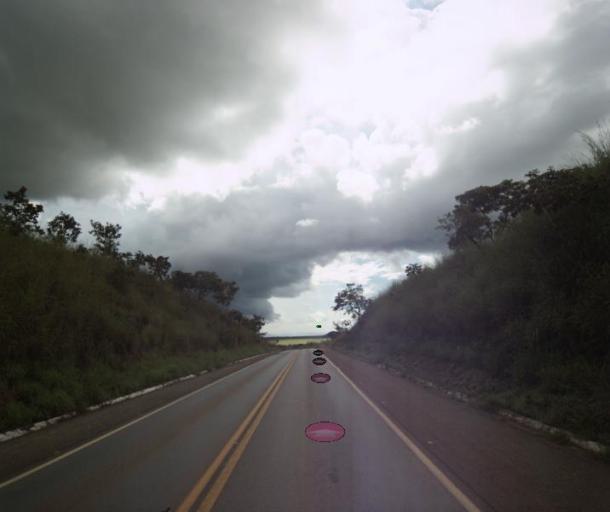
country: BR
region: Goias
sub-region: Uruacu
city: Uruacu
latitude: -14.6755
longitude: -49.1371
